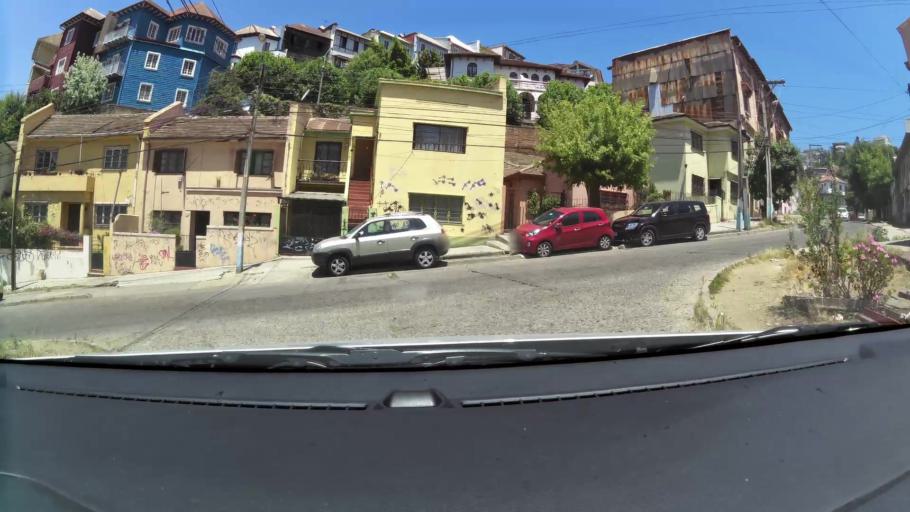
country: CL
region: Valparaiso
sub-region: Provincia de Valparaiso
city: Valparaiso
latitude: -33.0479
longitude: -71.6266
